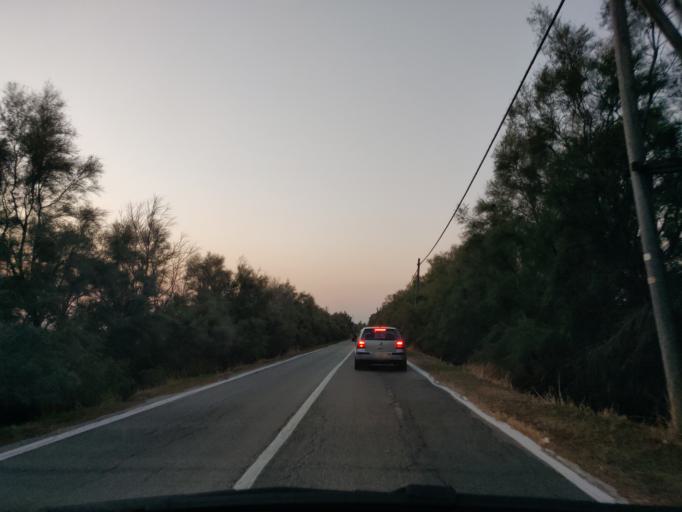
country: IT
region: Latium
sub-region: Citta metropolitana di Roma Capitale
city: Npp 23 (Parco Leonardo)
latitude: 41.8222
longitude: 12.2927
